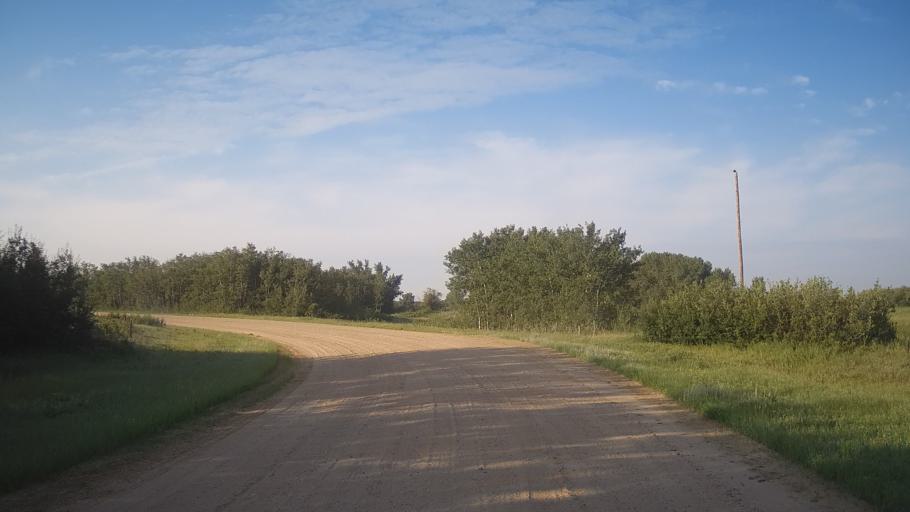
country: CA
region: Saskatchewan
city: Saskatoon
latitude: 51.8251
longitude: -106.5424
